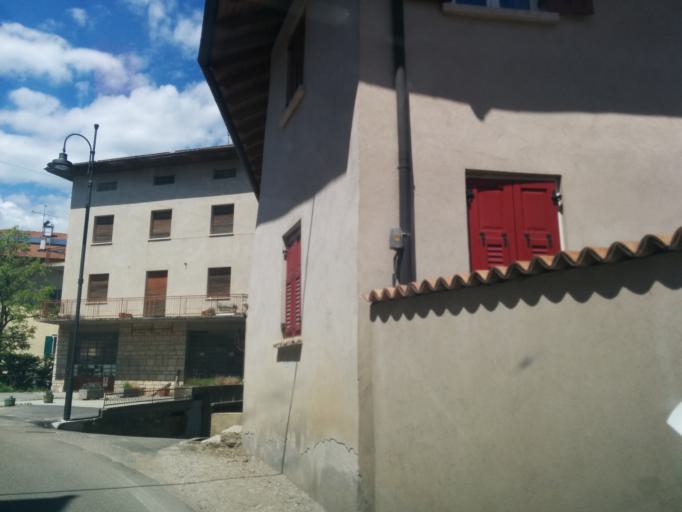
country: IT
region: Trentino-Alto Adige
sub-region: Provincia di Trento
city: Flavon
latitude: 46.3002
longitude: 11.0301
